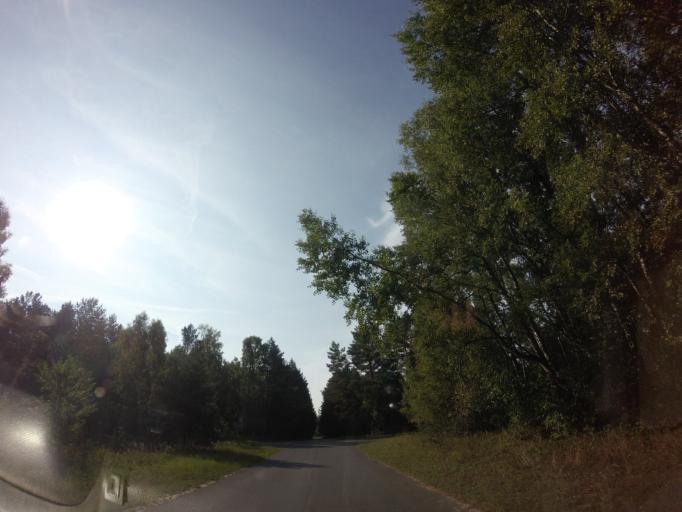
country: PL
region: West Pomeranian Voivodeship
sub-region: Powiat drawski
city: Drawsko Pomorskie
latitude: 53.4724
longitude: 15.7303
